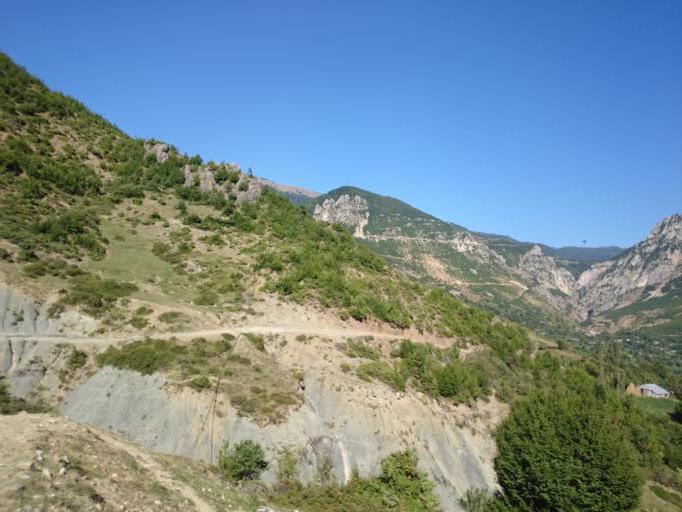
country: AL
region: Elbasan
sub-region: Rrethi i Gramshit
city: Kukur
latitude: 40.8676
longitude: 20.3490
